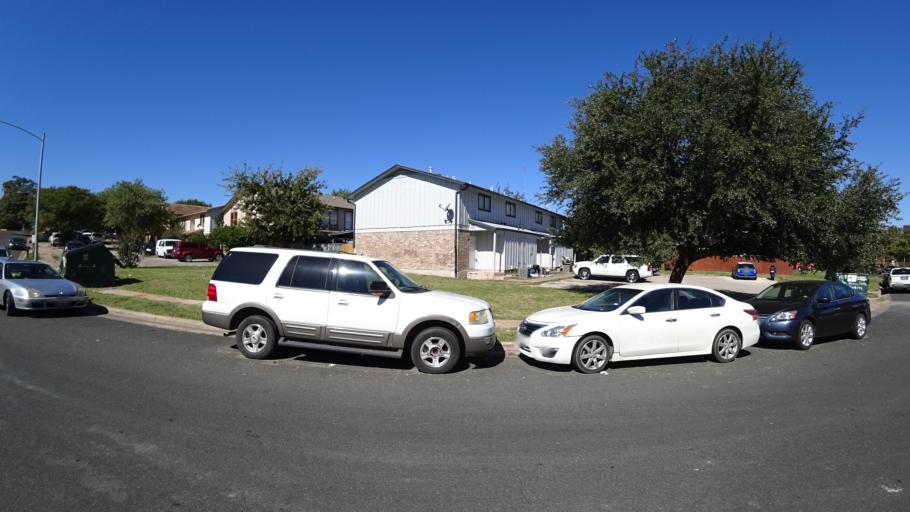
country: US
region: Texas
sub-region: Travis County
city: Rollingwood
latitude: 30.2322
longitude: -97.7757
